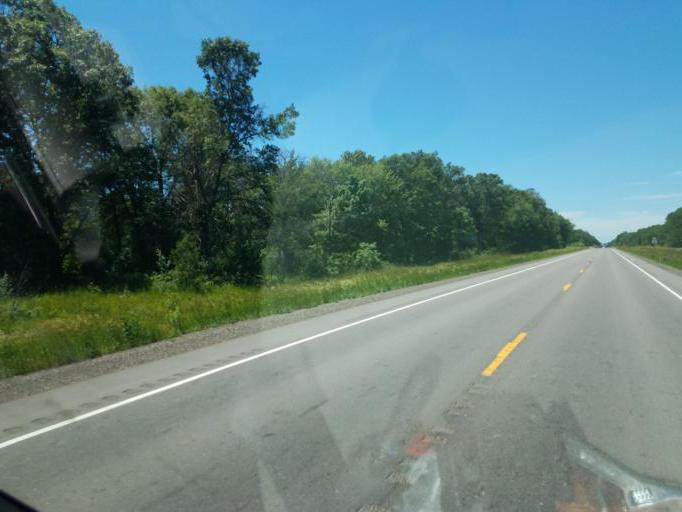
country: US
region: Wisconsin
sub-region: Juneau County
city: New Lisbon
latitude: 44.0256
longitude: -90.2317
